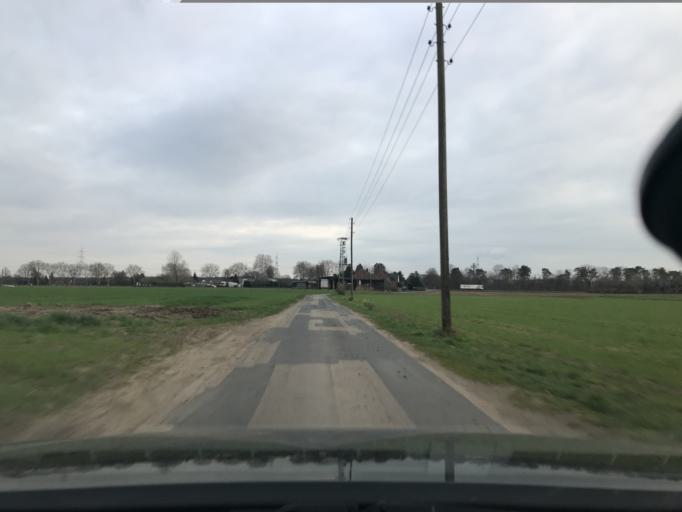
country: DE
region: North Rhine-Westphalia
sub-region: Regierungsbezirk Dusseldorf
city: Hunxe
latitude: 51.6705
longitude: 6.7092
